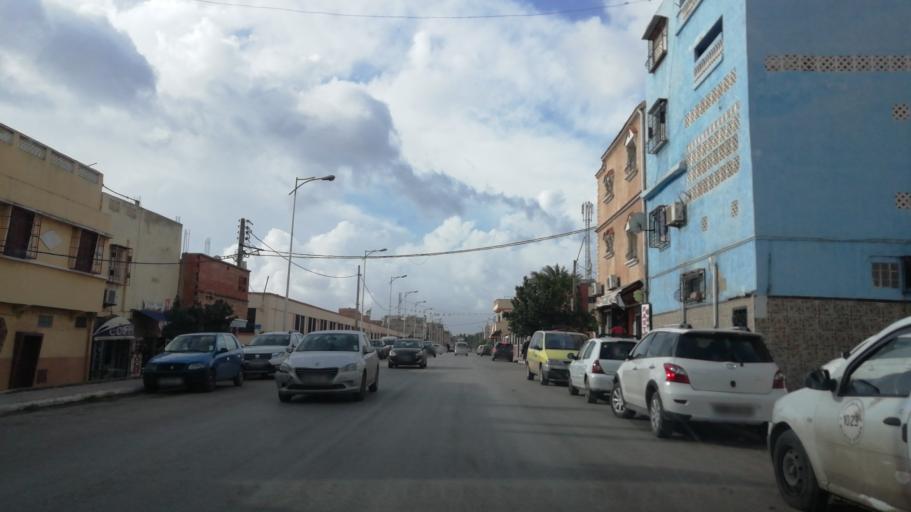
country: DZ
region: Oran
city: Oran
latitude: 35.6817
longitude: -0.6171
